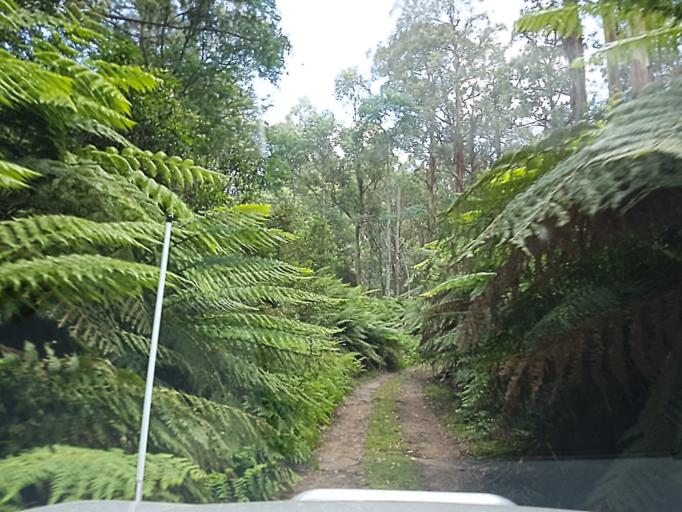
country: AU
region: Victoria
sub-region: East Gippsland
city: Lakes Entrance
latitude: -37.3480
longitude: 148.3197
